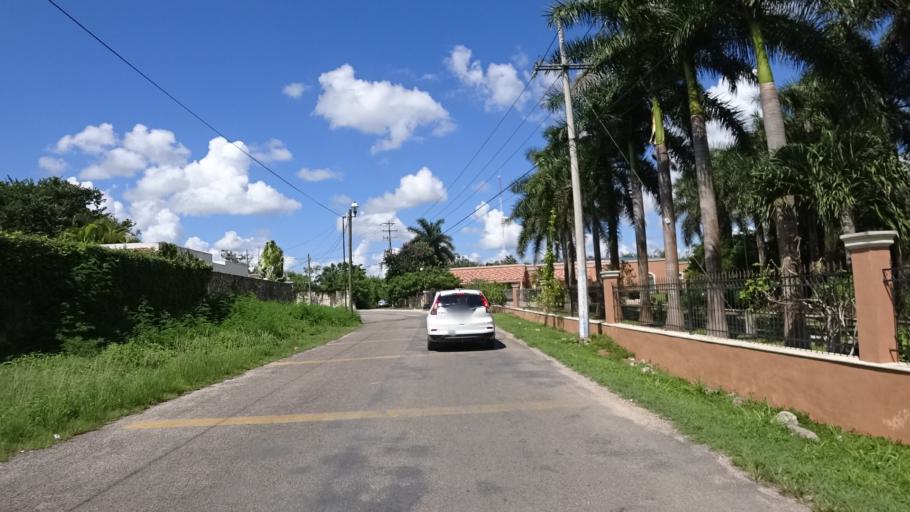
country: MX
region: Yucatan
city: Valladolid
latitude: 20.7022
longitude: -88.2002
